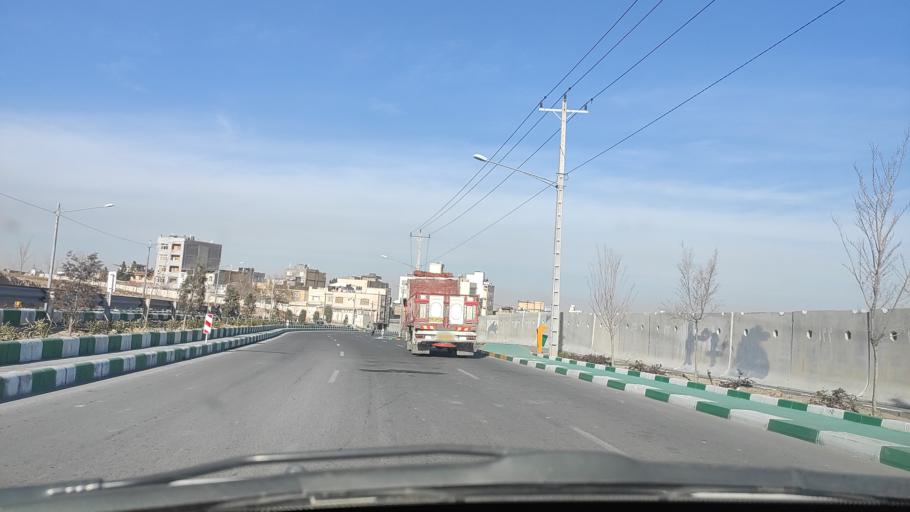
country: IR
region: Razavi Khorasan
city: Mashhad
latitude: 36.2841
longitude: 59.5310
